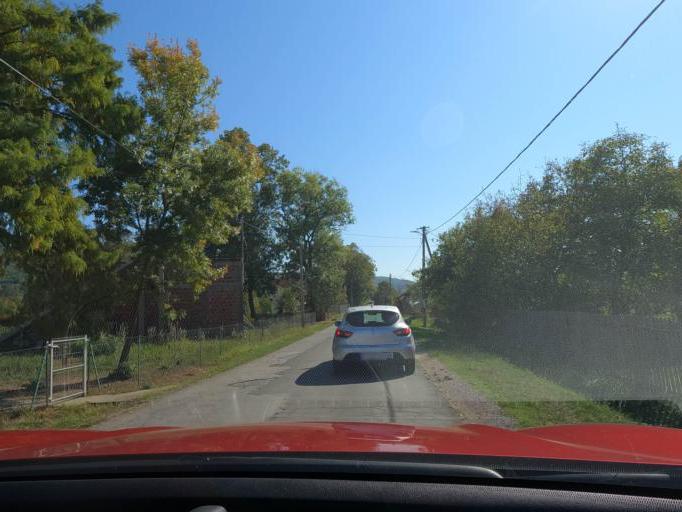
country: RS
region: Central Serbia
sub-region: Raski Okrug
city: Kraljevo
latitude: 43.7500
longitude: 20.7101
